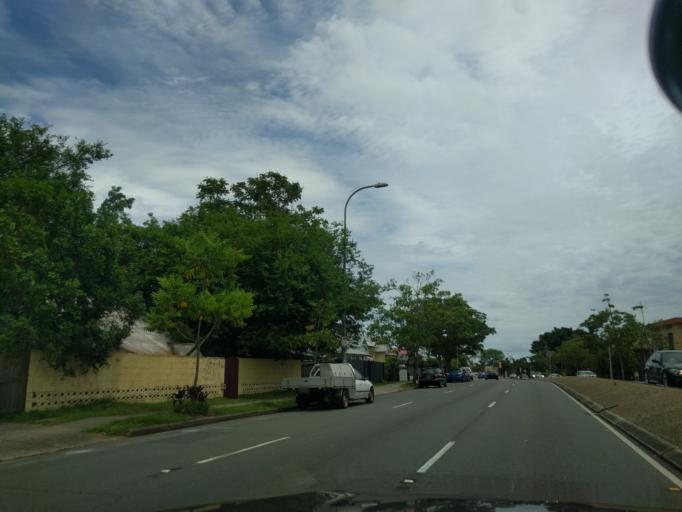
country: AU
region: Queensland
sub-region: Brisbane
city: Wilston
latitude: -27.4340
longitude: 153.0058
